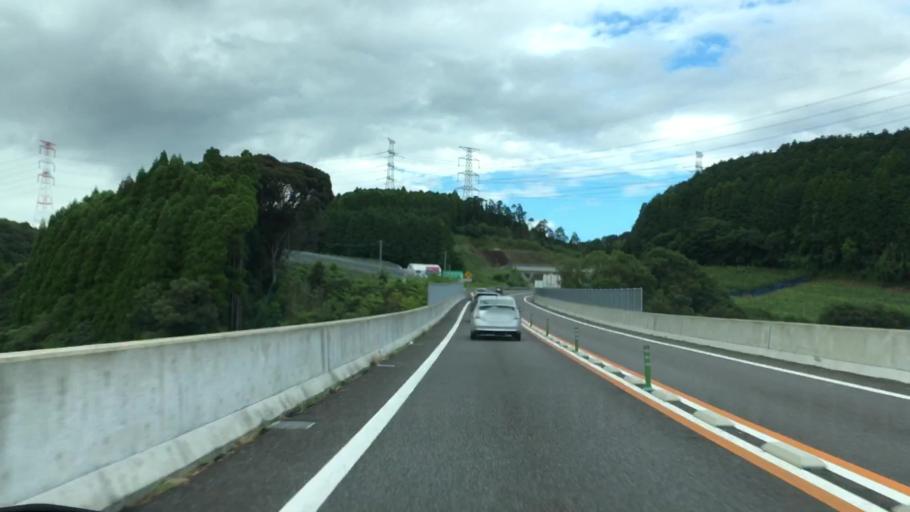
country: JP
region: Saga Prefecture
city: Imaricho-ko
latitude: 33.3487
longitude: 129.9246
